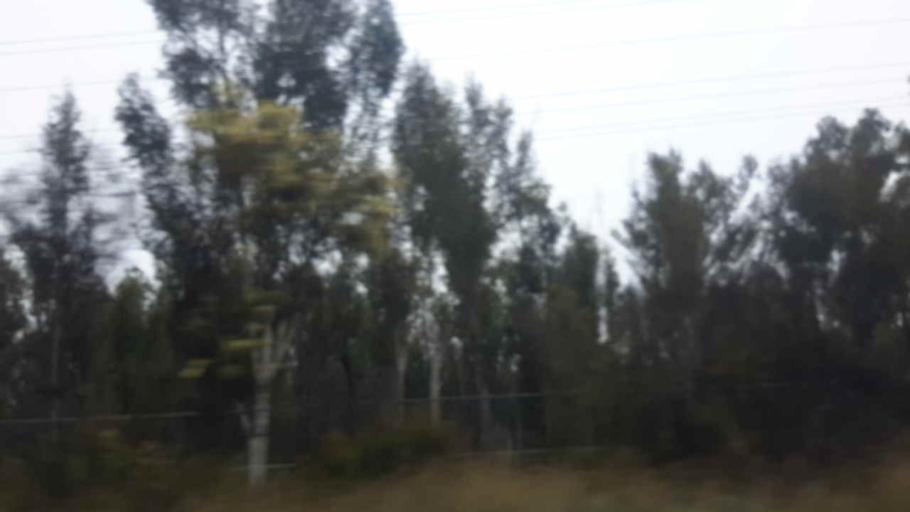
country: AU
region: New South Wales
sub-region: Penrith Municipality
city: Werrington Downs
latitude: -33.6832
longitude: 150.7388
